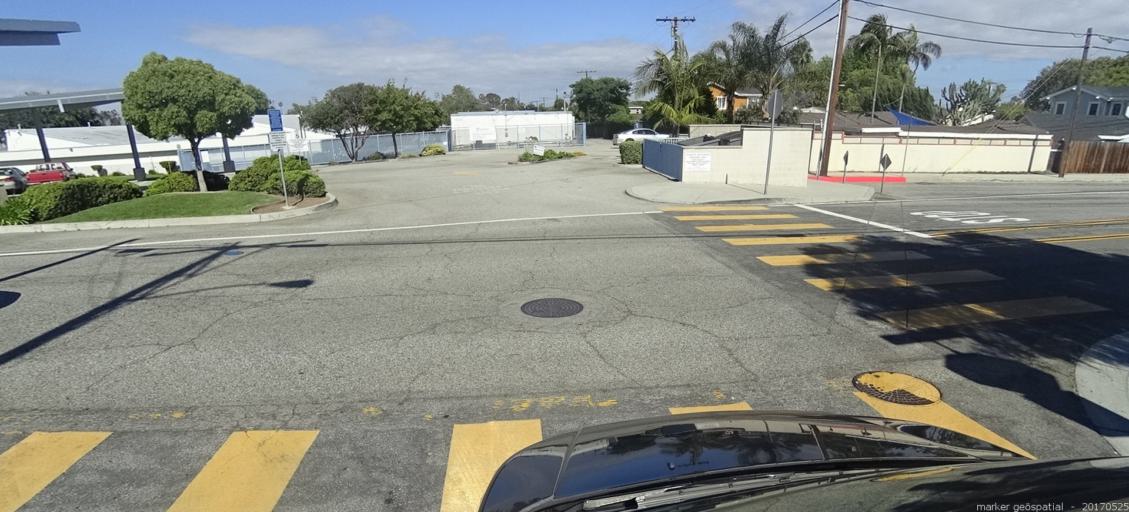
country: US
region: California
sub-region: Los Angeles County
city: Lawndale
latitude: 33.8638
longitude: -118.3657
